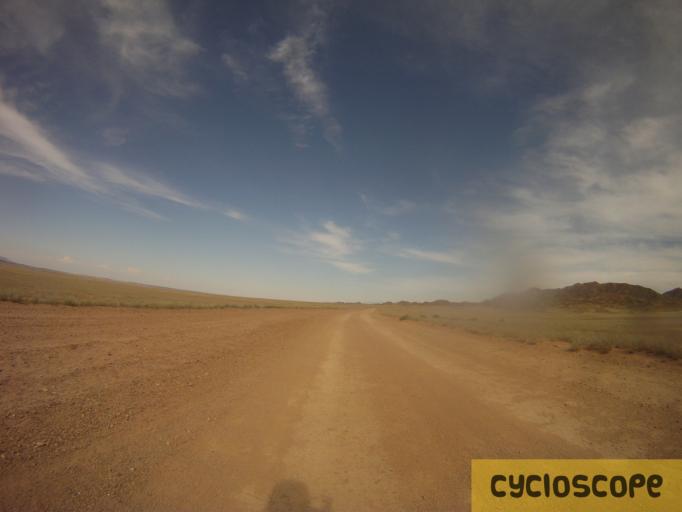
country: KZ
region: Almaty Oblysy
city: Kegen
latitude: 43.3566
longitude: 78.9668
